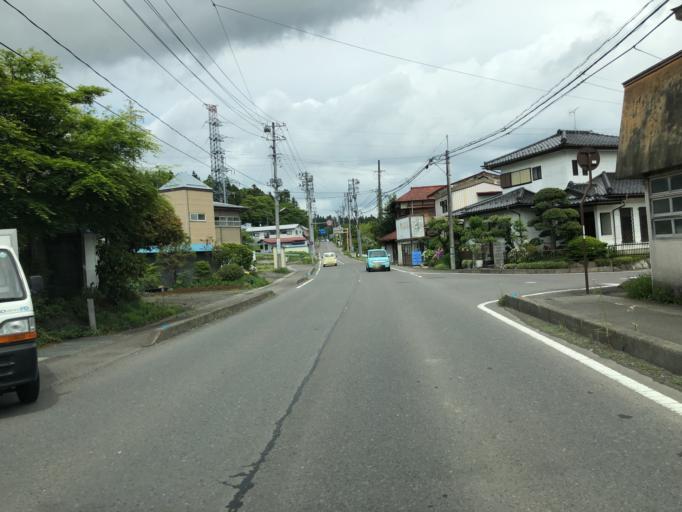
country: JP
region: Fukushima
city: Ishikawa
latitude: 37.0368
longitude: 140.3806
